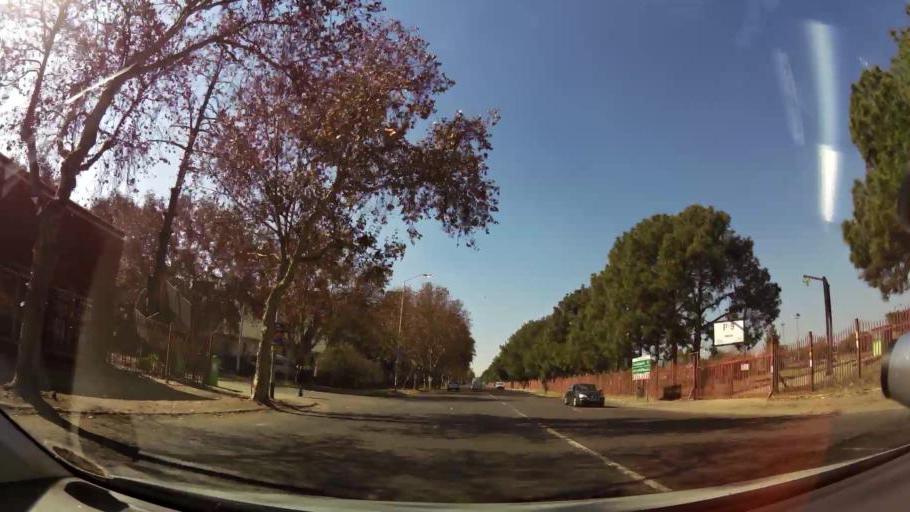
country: ZA
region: Gauteng
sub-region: City of Tshwane Metropolitan Municipality
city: Pretoria
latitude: -25.7480
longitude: 28.1646
